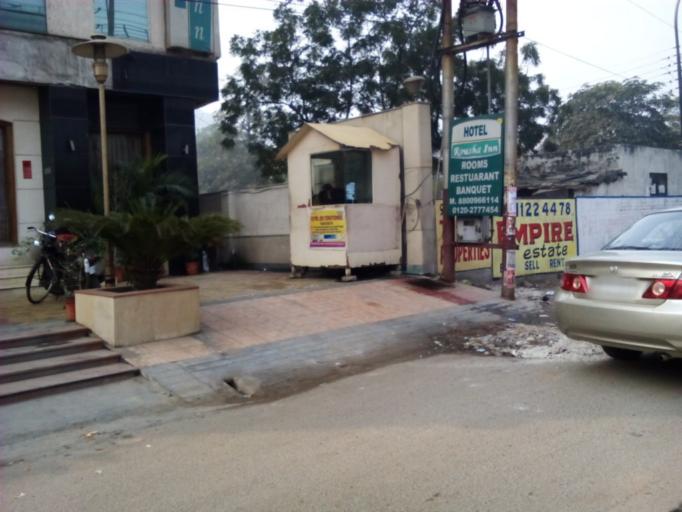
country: IN
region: Uttar Pradesh
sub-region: Gautam Buddha Nagar
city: Noida
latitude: 28.6452
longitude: 77.3232
